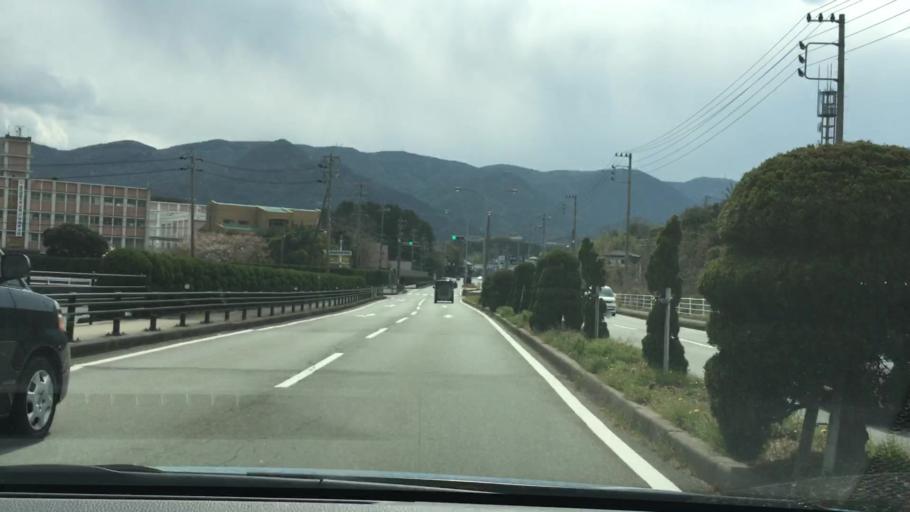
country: JP
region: Mie
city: Toba
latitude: 34.4841
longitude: 136.8256
